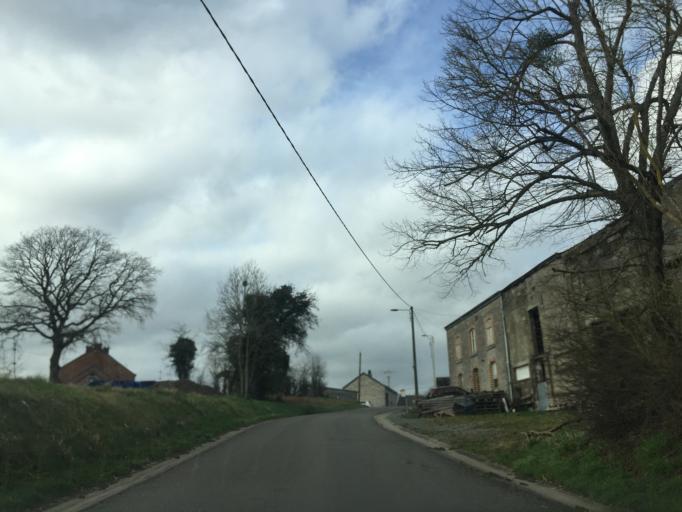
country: BE
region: Wallonia
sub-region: Province du Luxembourg
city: Durbuy
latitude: 50.3088
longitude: 5.4836
